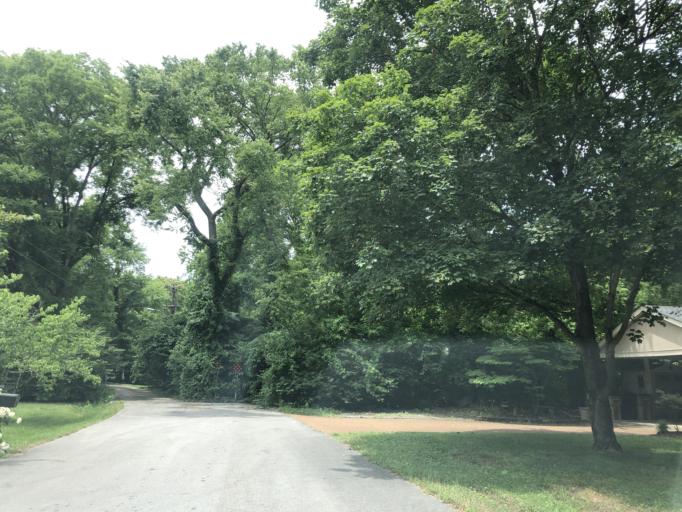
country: US
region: Tennessee
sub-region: Davidson County
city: Oak Hill
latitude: 36.1019
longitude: -86.7913
